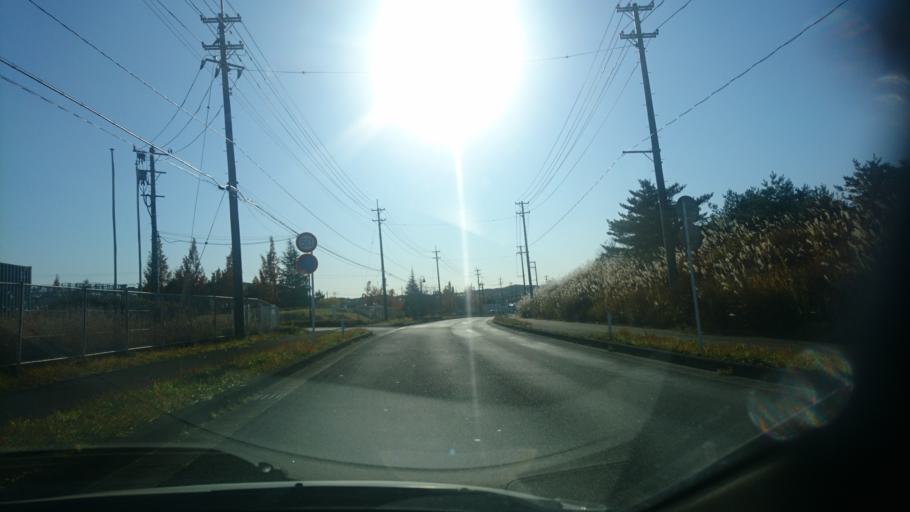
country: JP
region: Miyagi
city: Tomiya
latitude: 38.4571
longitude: 140.9360
